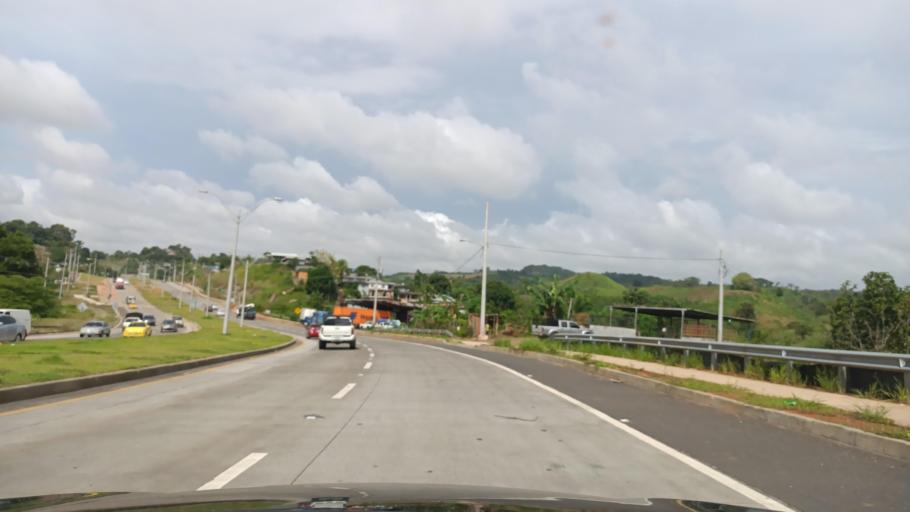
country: PA
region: Panama
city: Las Cumbres
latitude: 9.0994
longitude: -79.4885
